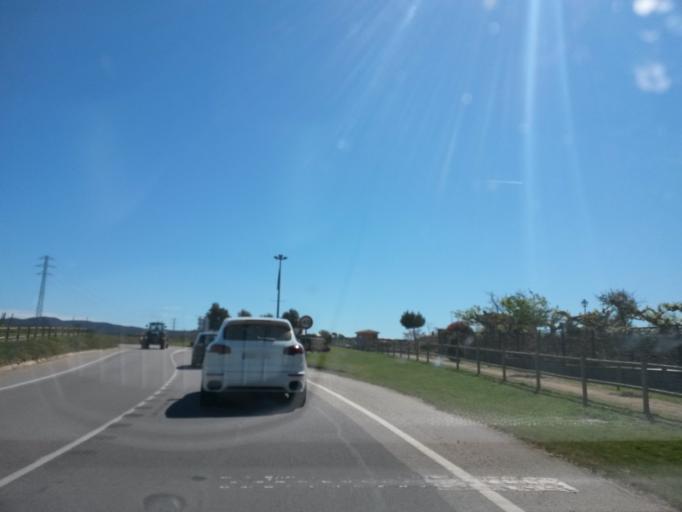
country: ES
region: Catalonia
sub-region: Provincia de Girona
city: Riudellots de la Selva
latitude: 41.8966
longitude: 2.8308
